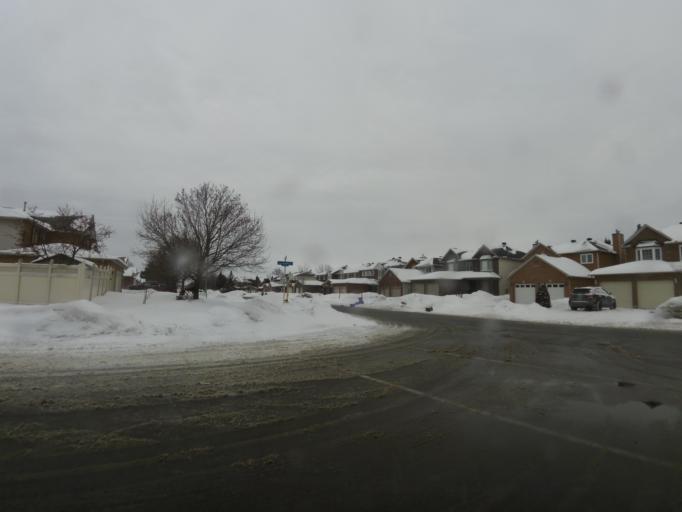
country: CA
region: Ontario
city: Ottawa
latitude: 45.3710
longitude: -75.6127
